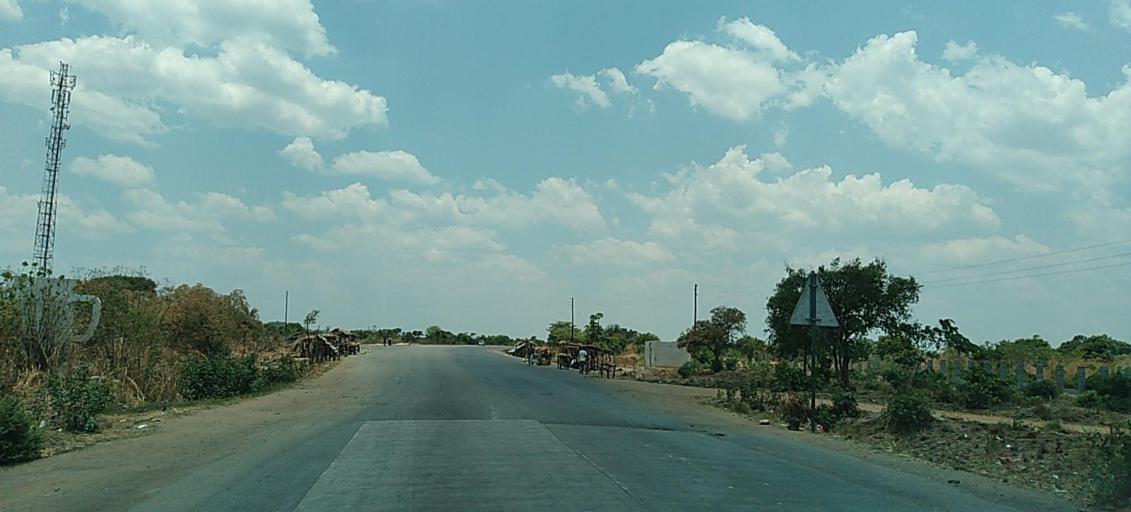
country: ZM
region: Central
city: Kapiri Mposhi
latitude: -13.8928
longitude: 28.6590
